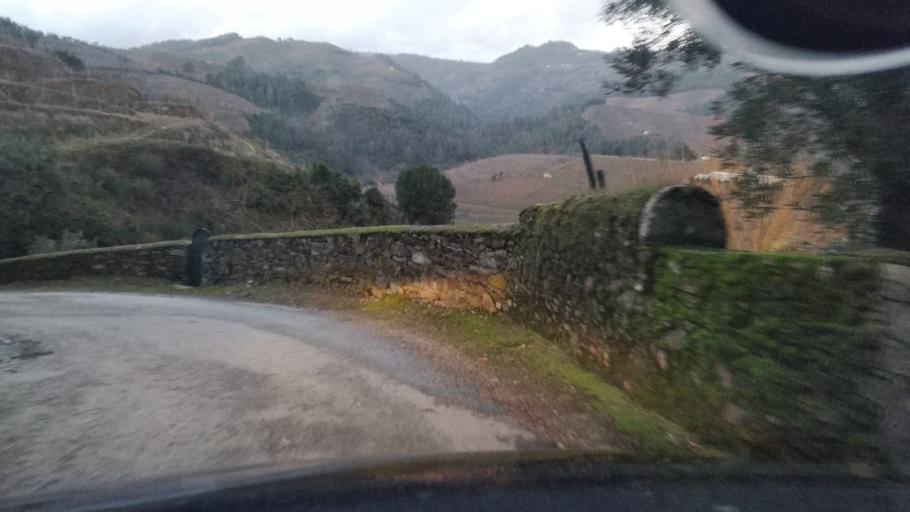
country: PT
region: Vila Real
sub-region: Santa Marta de Penaguiao
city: Santa Marta de Penaguiao
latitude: 41.2299
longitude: -7.7790
